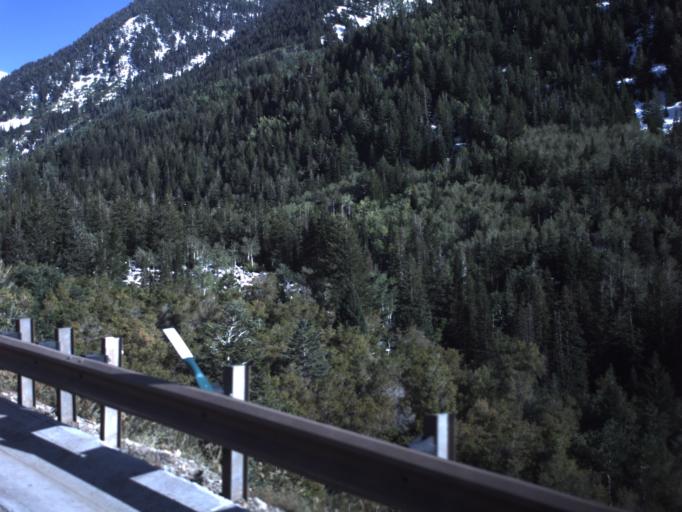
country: US
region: Utah
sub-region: Salt Lake County
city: Granite
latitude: 40.5736
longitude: -111.6978
